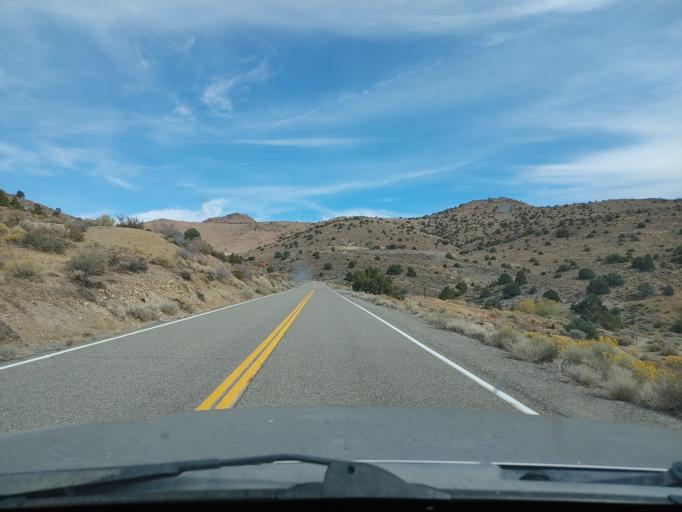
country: US
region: Nevada
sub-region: Storey County
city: Virginia City
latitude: 39.2635
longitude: -119.6341
